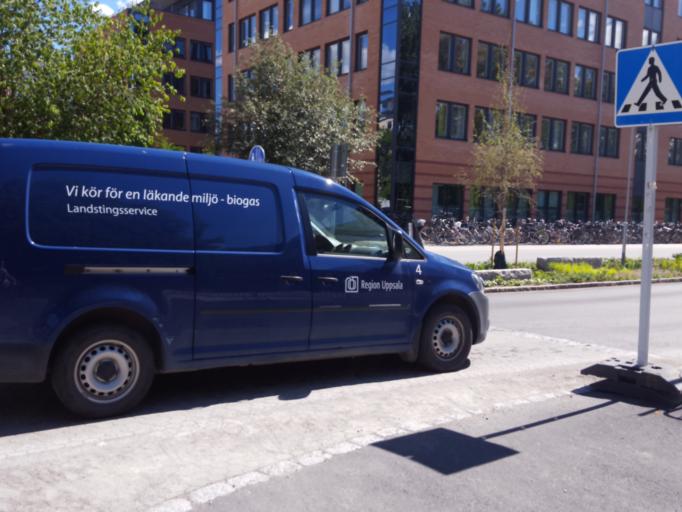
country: SE
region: Uppsala
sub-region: Uppsala Kommun
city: Uppsala
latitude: 59.8532
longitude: 17.6478
